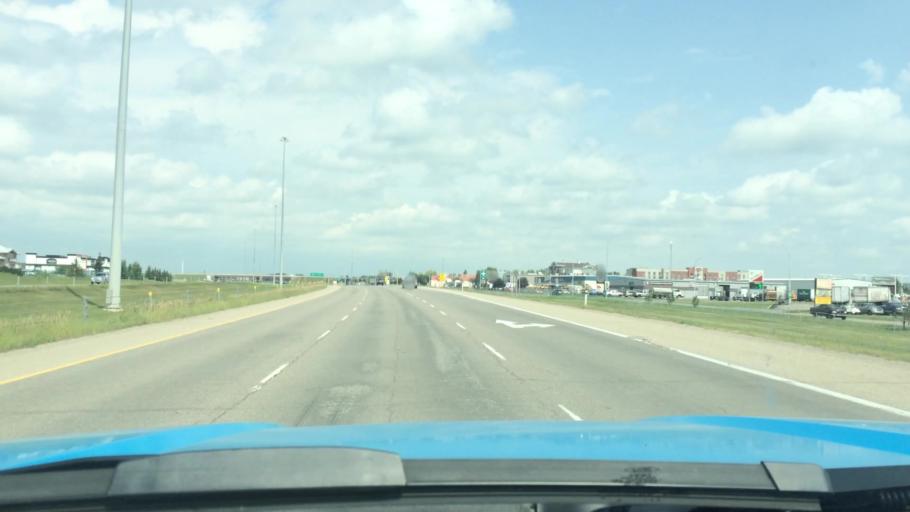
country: CA
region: Alberta
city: Airdrie
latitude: 51.2911
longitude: -113.9997
